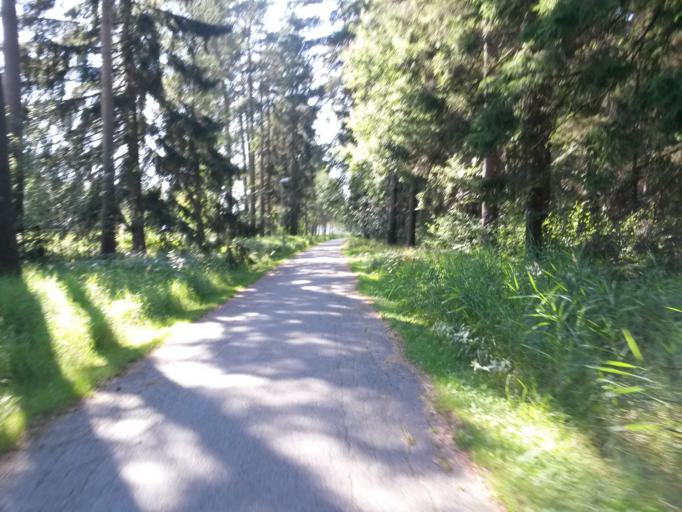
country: SE
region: Vaestra Goetaland
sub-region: Lidkopings Kommun
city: Lidkoping
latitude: 58.4937
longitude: 13.2174
